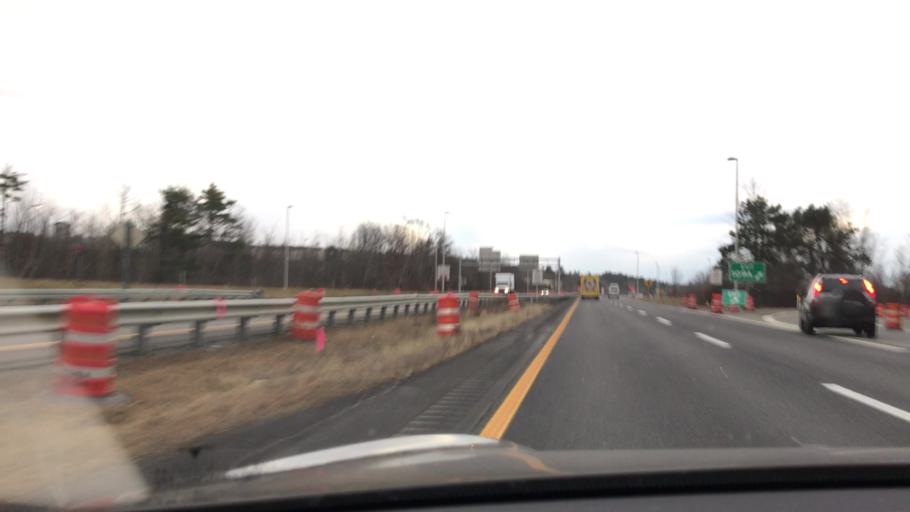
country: US
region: Maine
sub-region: Kennebec County
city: Augusta
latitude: 44.3127
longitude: -69.8098
